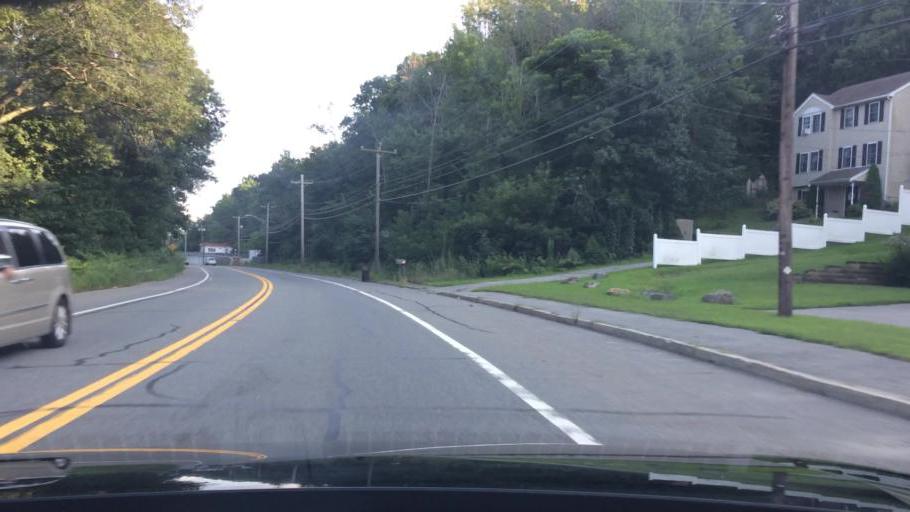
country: US
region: Massachusetts
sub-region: Essex County
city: Haverhill
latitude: 42.7698
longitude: -71.1328
